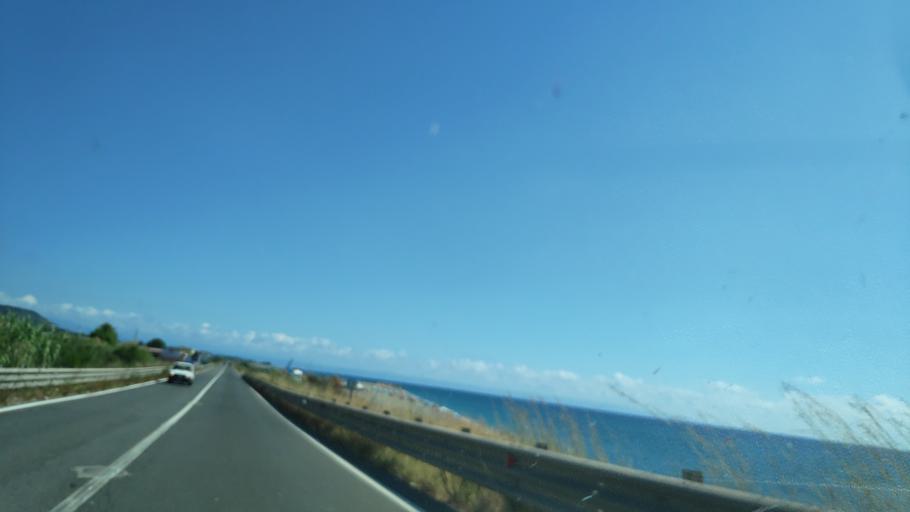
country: IT
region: Calabria
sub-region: Provincia di Cosenza
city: Campora San Giovanni
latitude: 39.0640
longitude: 16.0907
